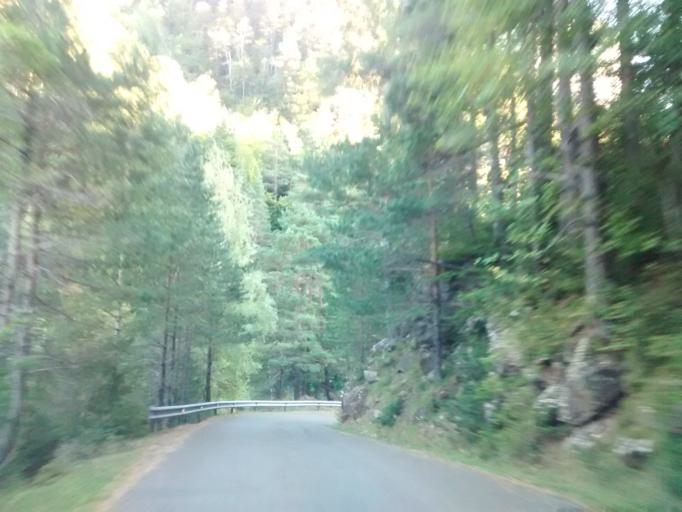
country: ES
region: Aragon
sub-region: Provincia de Huesca
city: Aragues del Puerto
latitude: 42.8094
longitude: -0.7122
